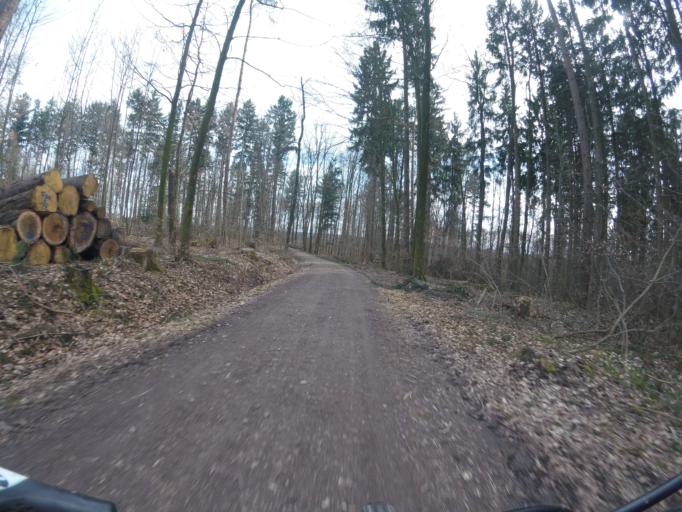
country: DE
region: Baden-Wuerttemberg
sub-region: Regierungsbezirk Stuttgart
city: Aspach
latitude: 48.9715
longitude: 9.4247
